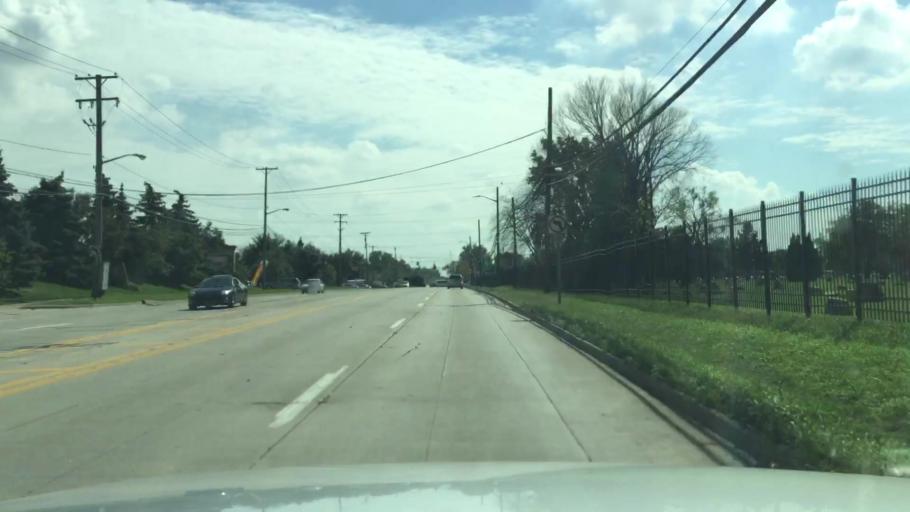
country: US
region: Michigan
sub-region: Wayne County
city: Wayne
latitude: 42.2878
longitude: -83.3489
